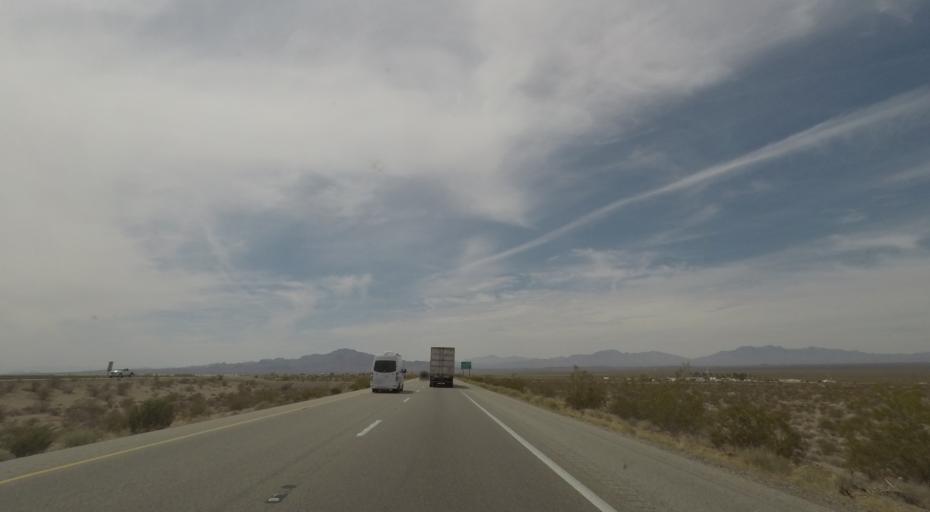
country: US
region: California
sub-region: San Bernardino County
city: Needles
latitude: 34.8146
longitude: -115.1739
